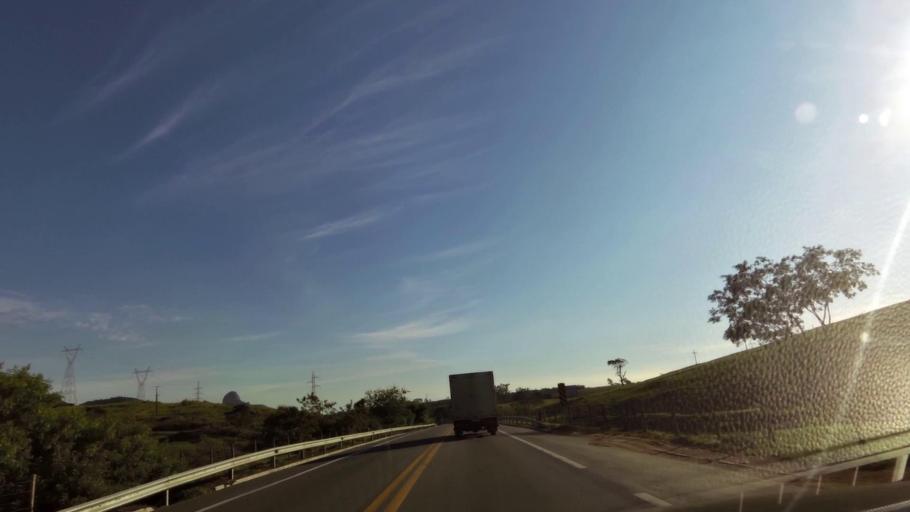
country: BR
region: Espirito Santo
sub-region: Guarapari
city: Guarapari
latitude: -20.5628
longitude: -40.4813
